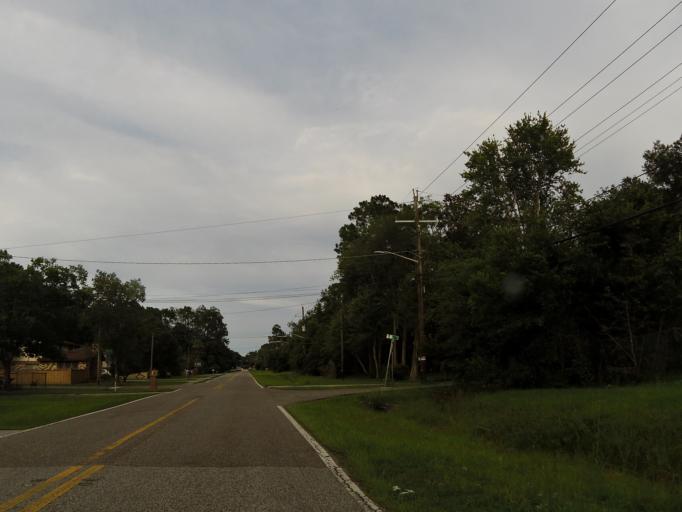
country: US
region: Florida
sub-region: Duval County
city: Jacksonville
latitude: 30.3943
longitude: -81.7415
